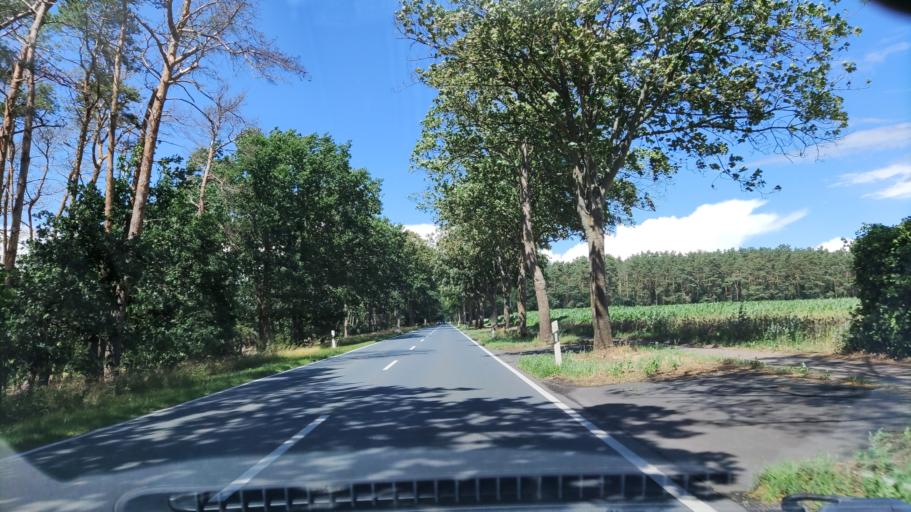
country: DE
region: Lower Saxony
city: Eickeloh
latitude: 52.7382
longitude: 9.6013
